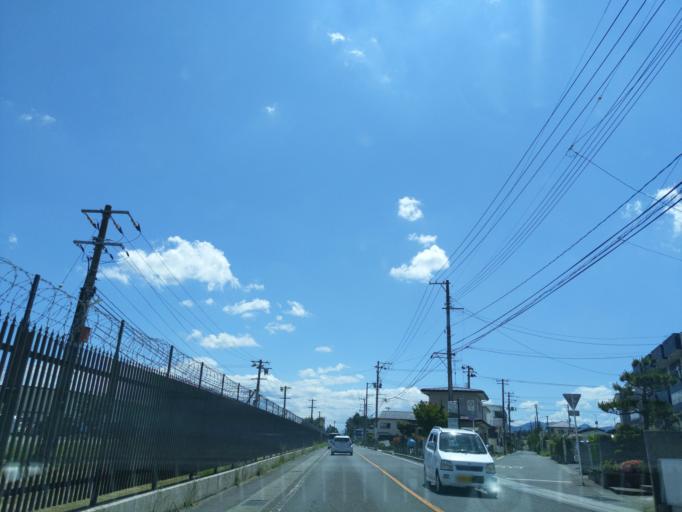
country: JP
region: Fukushima
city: Koriyama
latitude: 37.3989
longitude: 140.3241
